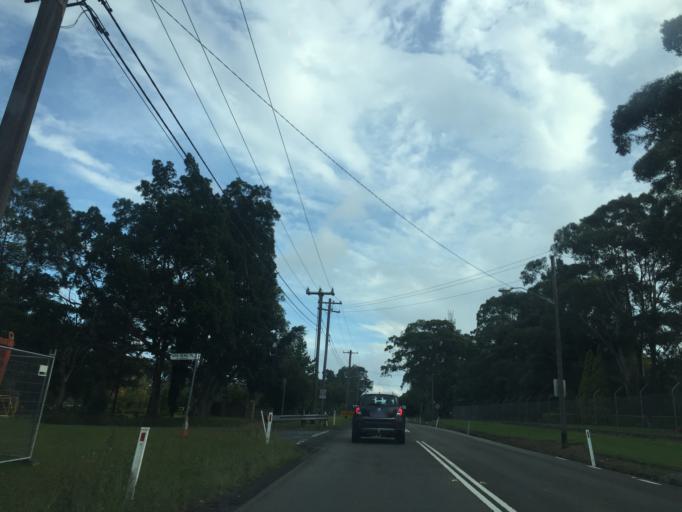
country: AU
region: New South Wales
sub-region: Hornsby Shire
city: Galston
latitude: -33.6748
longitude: 151.0333
